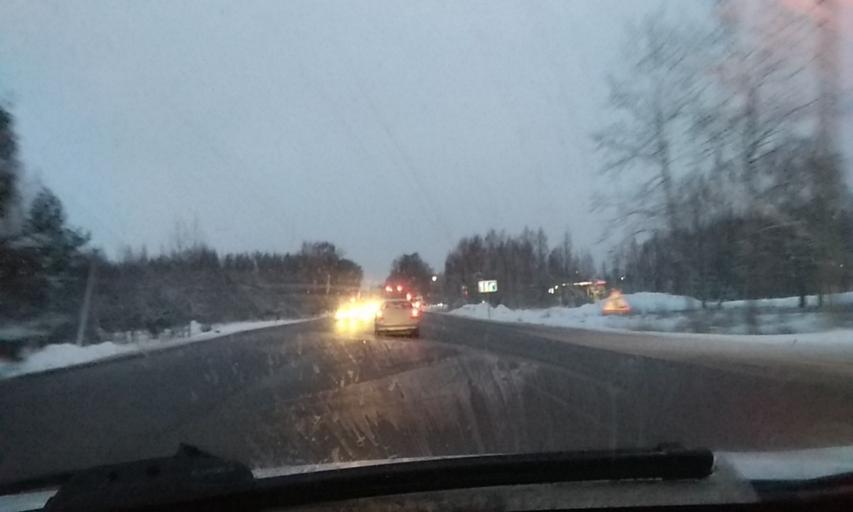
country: LT
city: Ramuciai
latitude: 54.9192
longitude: 24.0429
